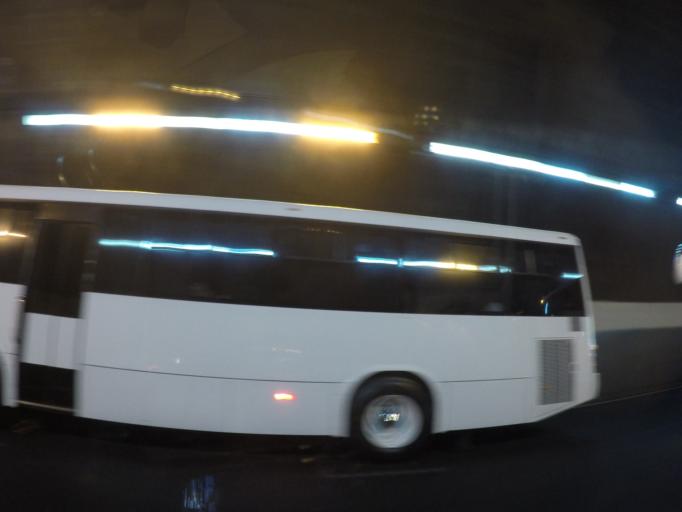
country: MX
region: Mexico City
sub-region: Cuajimalpa de Morelos
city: San Lorenzo Acopilco
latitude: 19.3176
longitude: -99.3232
